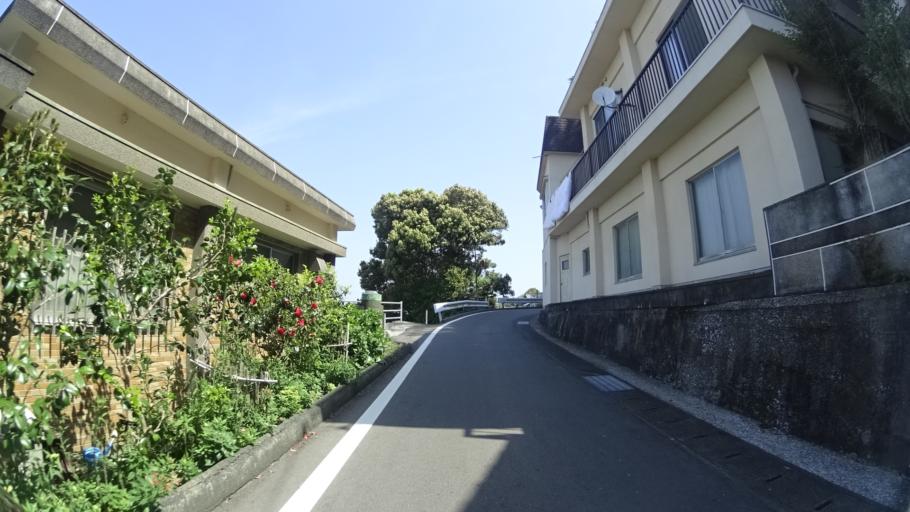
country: JP
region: Ehime
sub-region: Nishiuwa-gun
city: Ikata-cho
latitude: 33.3711
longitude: 132.0523
